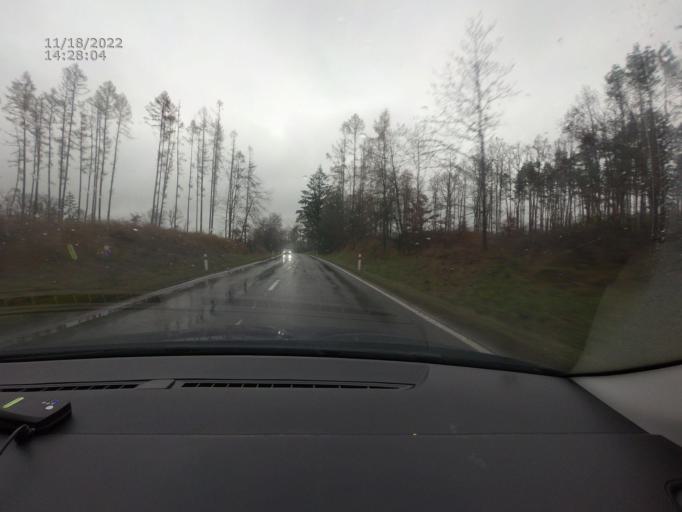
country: CZ
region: Jihocesky
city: Kovarov
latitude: 49.4226
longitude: 14.2105
